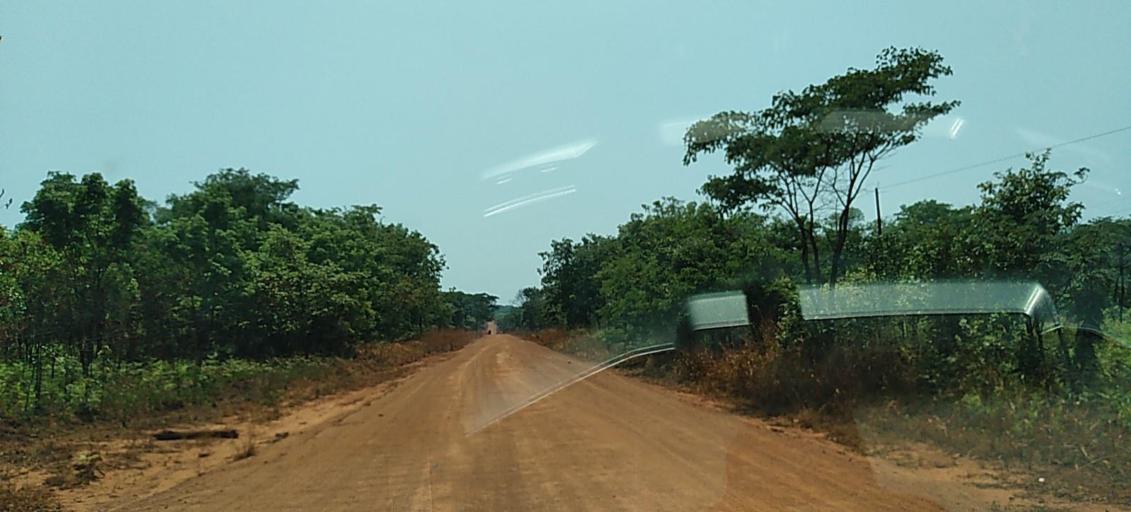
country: ZM
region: North-Western
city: Kansanshi
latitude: -11.9874
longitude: 26.8479
